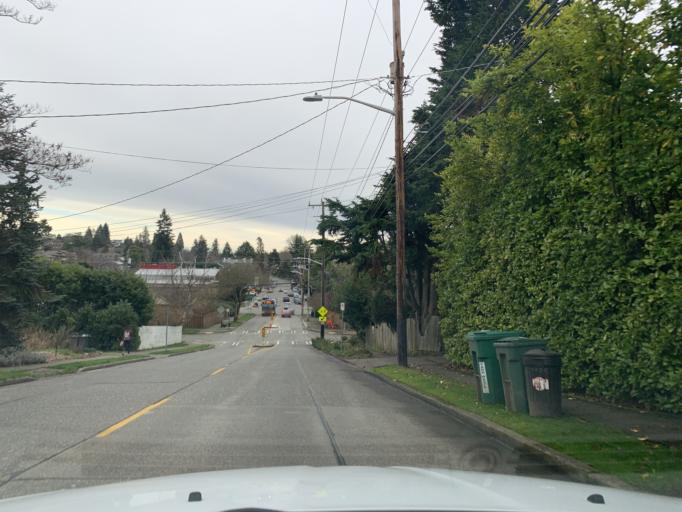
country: US
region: Washington
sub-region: King County
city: Yarrow Point
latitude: 47.6685
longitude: -122.2866
